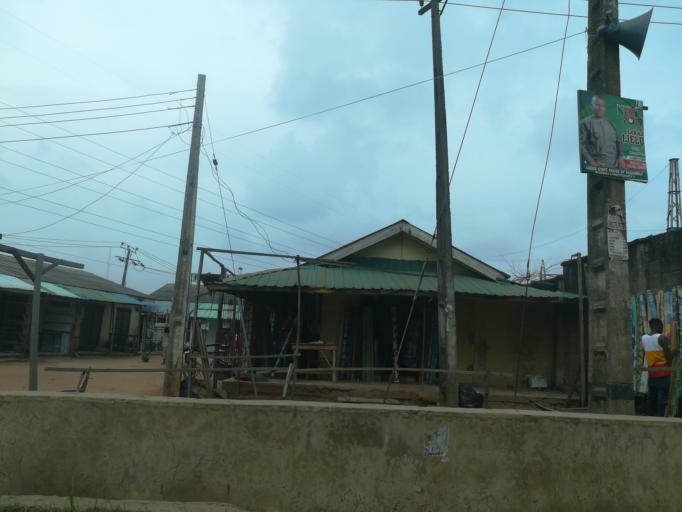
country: NG
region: Lagos
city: Ikorodu
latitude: 6.6244
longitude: 3.5066
